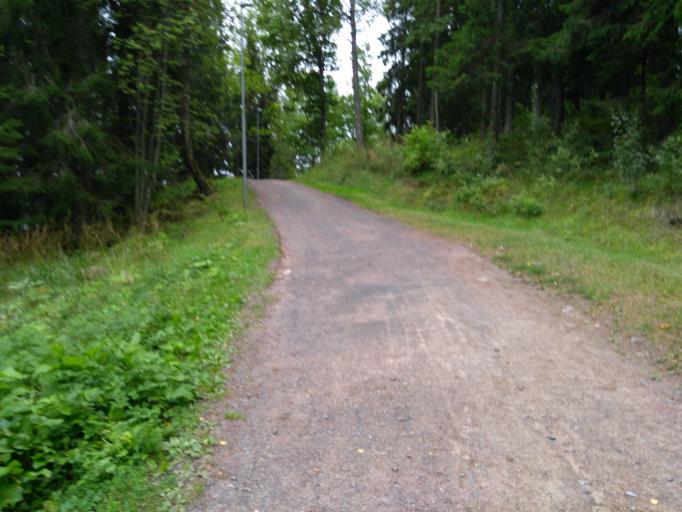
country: SE
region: Vaestra Goetaland
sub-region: Skovde Kommun
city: Skoevde
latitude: 58.4039
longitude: 13.8063
